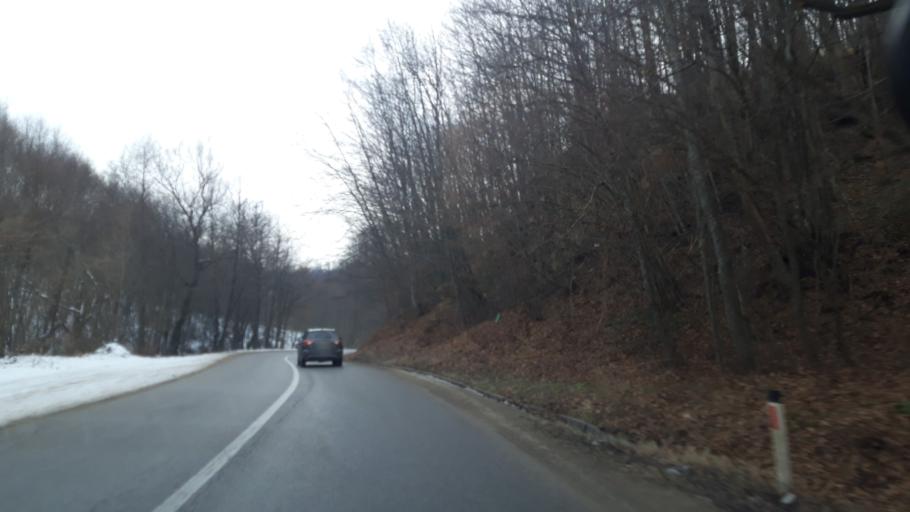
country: BA
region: Republika Srpska
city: Vlasenica
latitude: 44.1816
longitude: 19.0085
